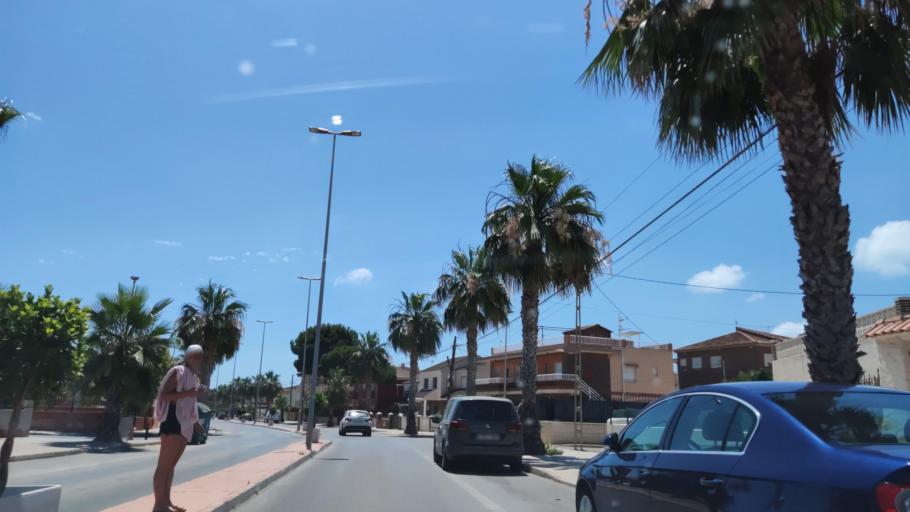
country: ES
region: Murcia
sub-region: Murcia
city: Los Alcazares
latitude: 37.7580
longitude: -0.8367
